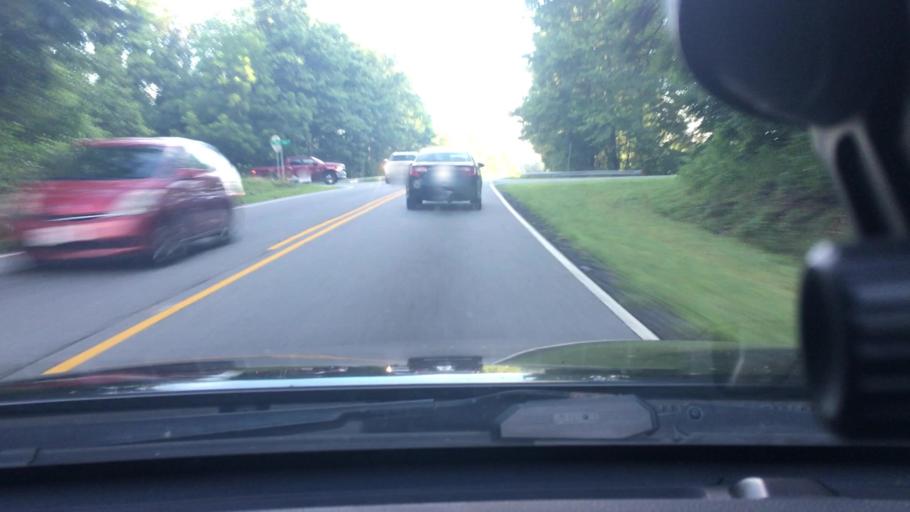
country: US
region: North Carolina
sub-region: McDowell County
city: West Marion
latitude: 35.5860
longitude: -81.9824
